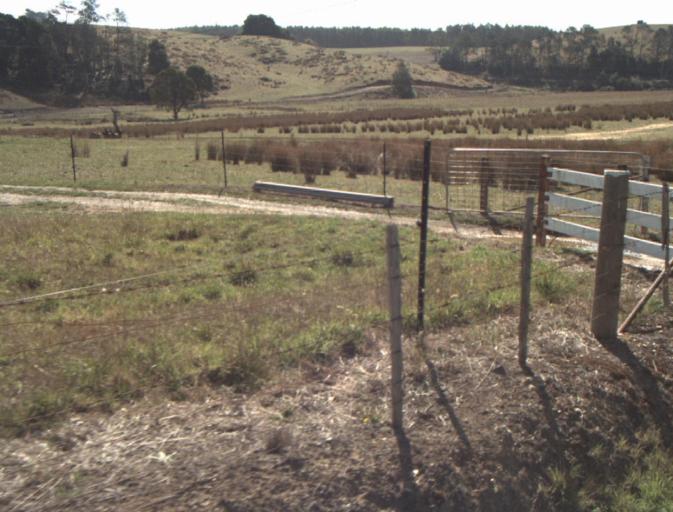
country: AU
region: Tasmania
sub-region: Launceston
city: Mayfield
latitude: -41.2267
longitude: 147.2365
